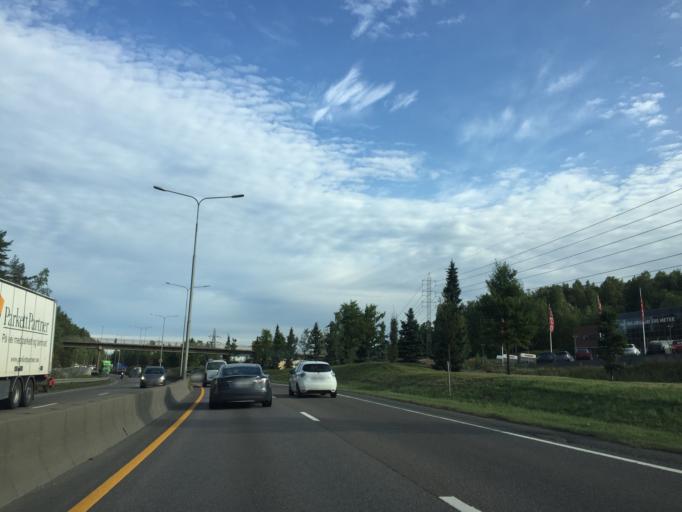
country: NO
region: Akershus
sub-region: Oppegard
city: Kolbotn
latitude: 59.8689
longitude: 10.8294
